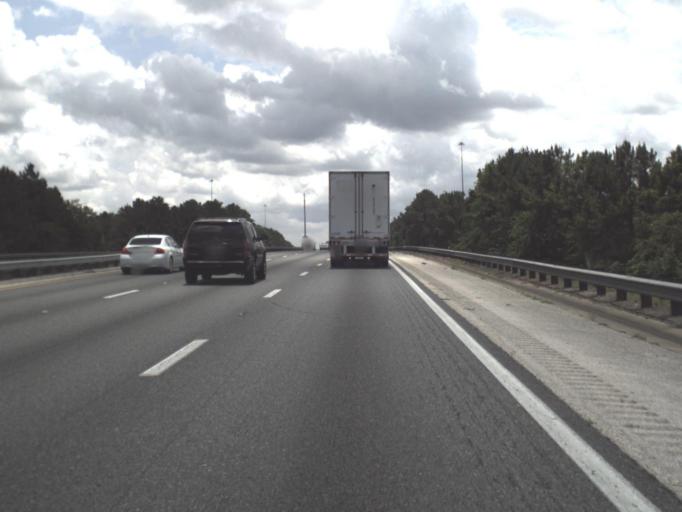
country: US
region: Florida
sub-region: Alachua County
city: Gainesville
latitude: 29.6191
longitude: -82.3876
